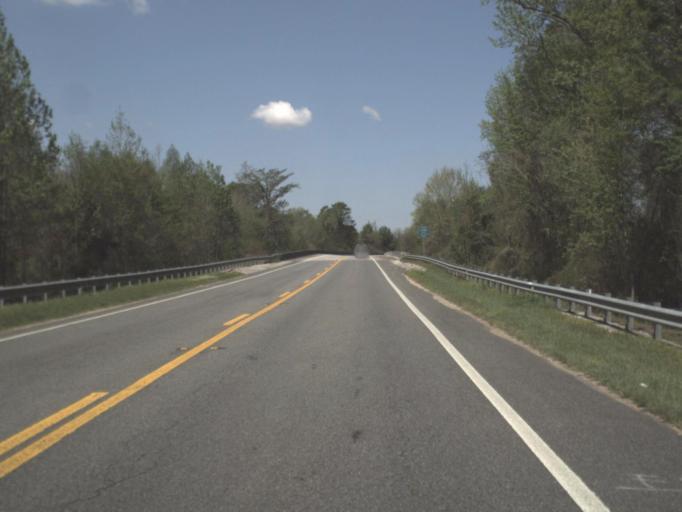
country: US
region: Florida
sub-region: Escambia County
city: Century
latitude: 30.9569
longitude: -87.2250
